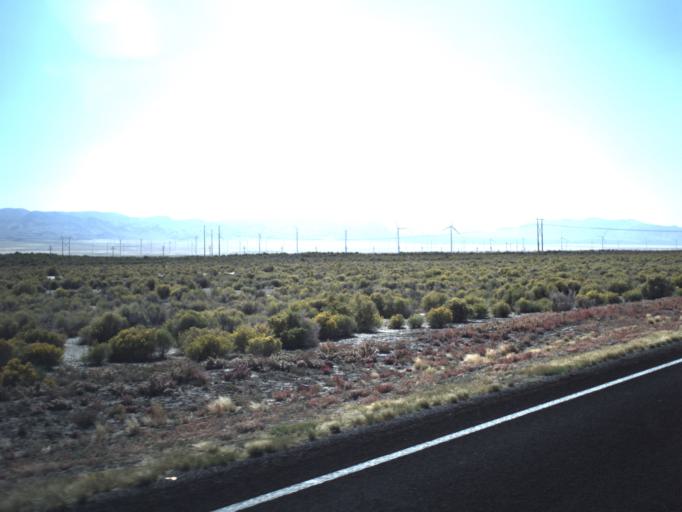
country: US
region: Utah
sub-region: Beaver County
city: Milford
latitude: 38.5786
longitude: -112.9893
